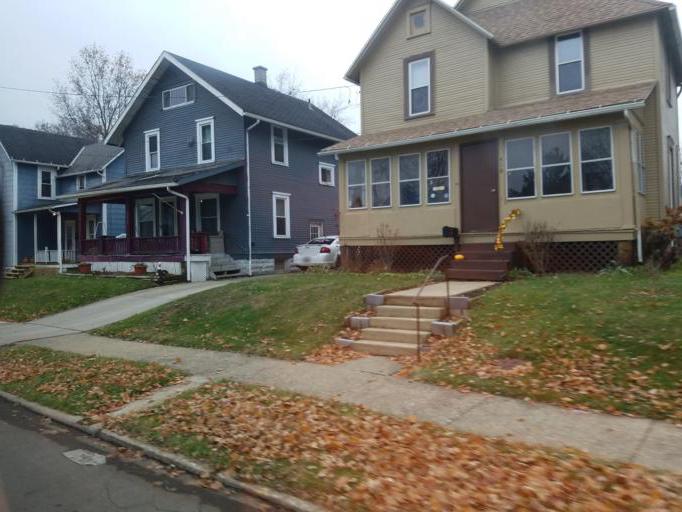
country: US
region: Ohio
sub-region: Richland County
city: Mansfield
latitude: 40.7467
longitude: -82.5151
